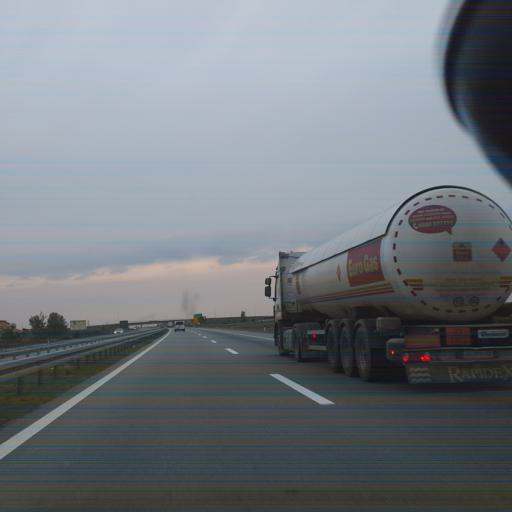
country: RS
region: Autonomna Pokrajina Vojvodina
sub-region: Juznobacki Okrug
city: Kovilj
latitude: 45.2360
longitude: 20.0443
